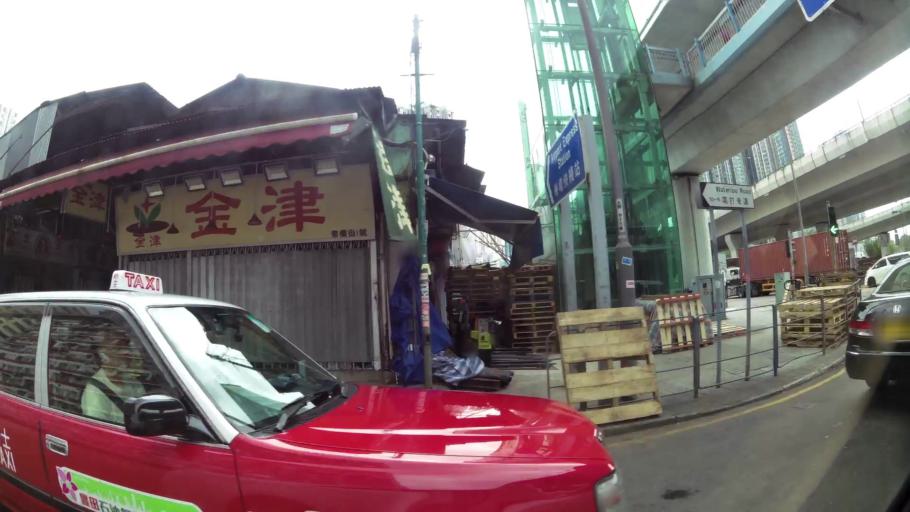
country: HK
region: Kowloon City
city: Kowloon
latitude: 22.3124
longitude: 114.1676
